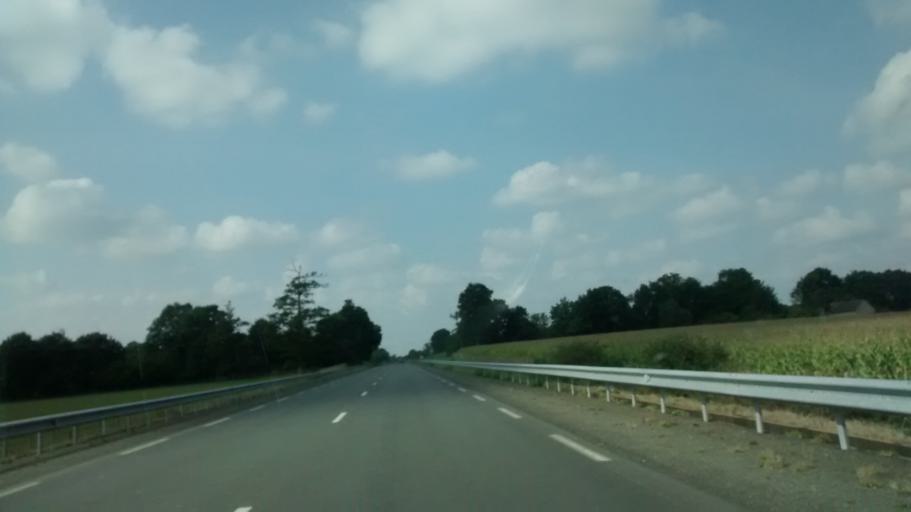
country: FR
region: Brittany
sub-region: Departement d'Ille-et-Vilaine
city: Livre-sur-Changeon
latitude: 48.2409
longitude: -1.3714
